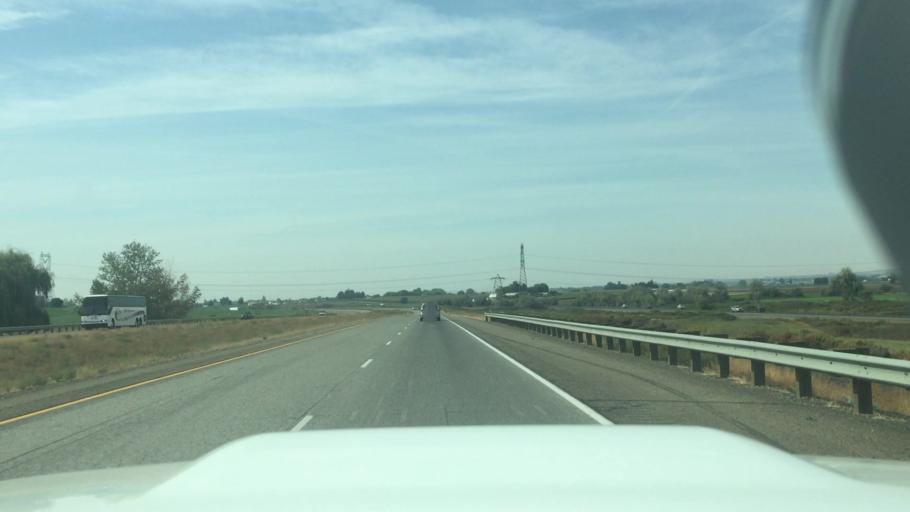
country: US
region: Washington
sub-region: Yakima County
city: Granger
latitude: 46.3347
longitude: -120.1269
